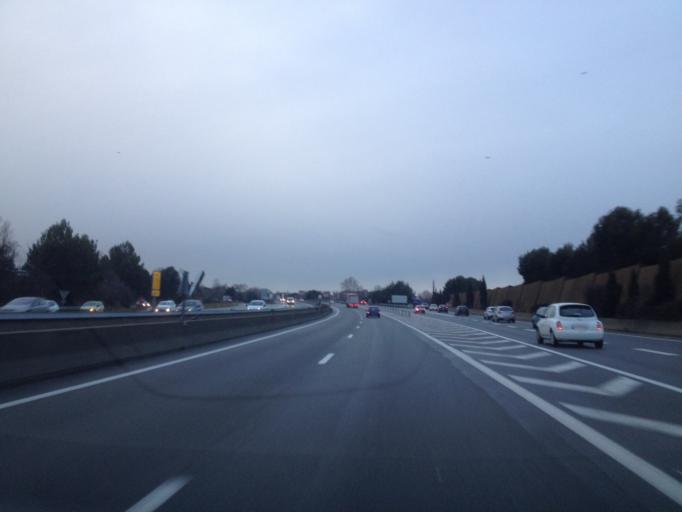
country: FR
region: Provence-Alpes-Cote d'Azur
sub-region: Departement des Bouches-du-Rhone
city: Aix-en-Provence
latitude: 43.5173
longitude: 5.4317
